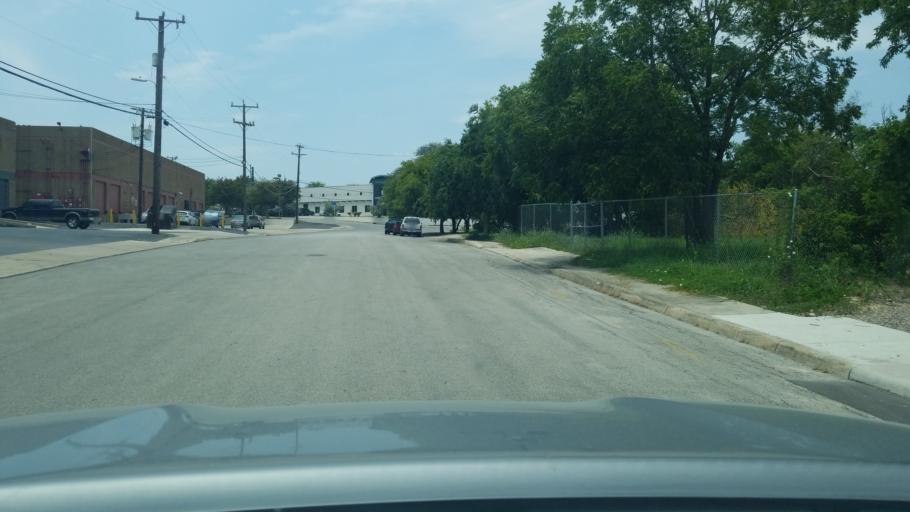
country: US
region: Texas
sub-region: Bexar County
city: Castle Hills
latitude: 29.5290
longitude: -98.4892
